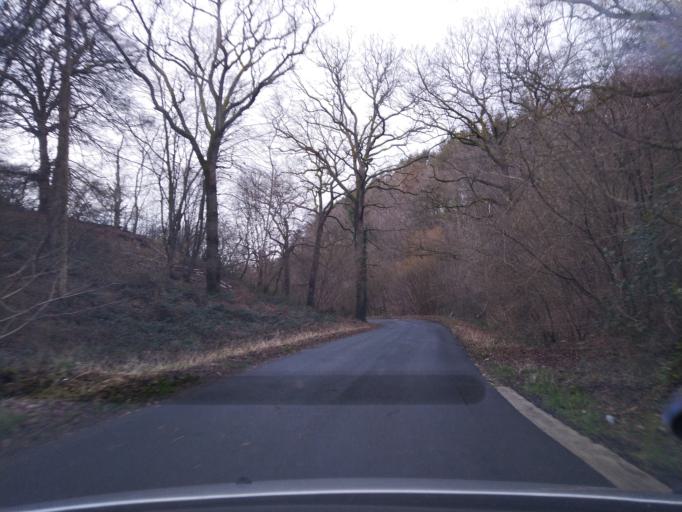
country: FR
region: Haute-Normandie
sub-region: Departement de la Seine-Maritime
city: Duclair
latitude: 49.4901
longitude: 0.9038
